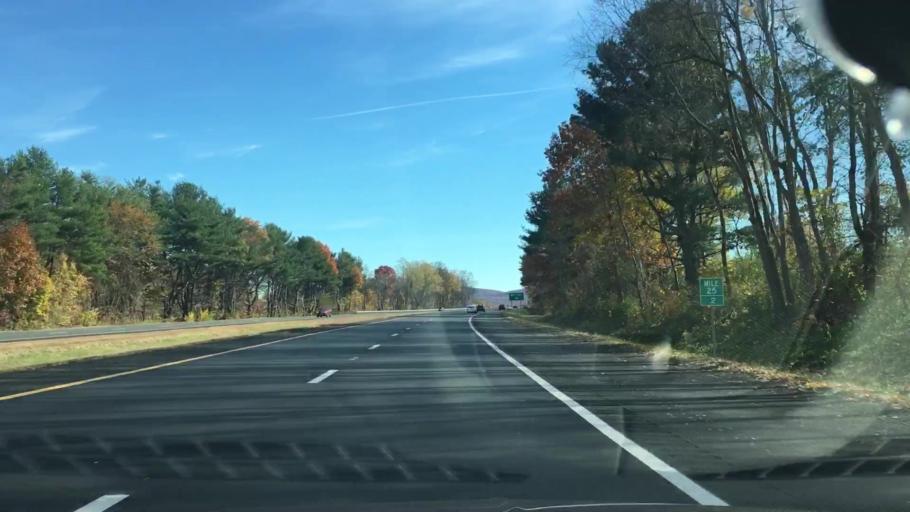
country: US
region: Massachusetts
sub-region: Hampshire County
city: Northampton
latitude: 42.3369
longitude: -72.6283
